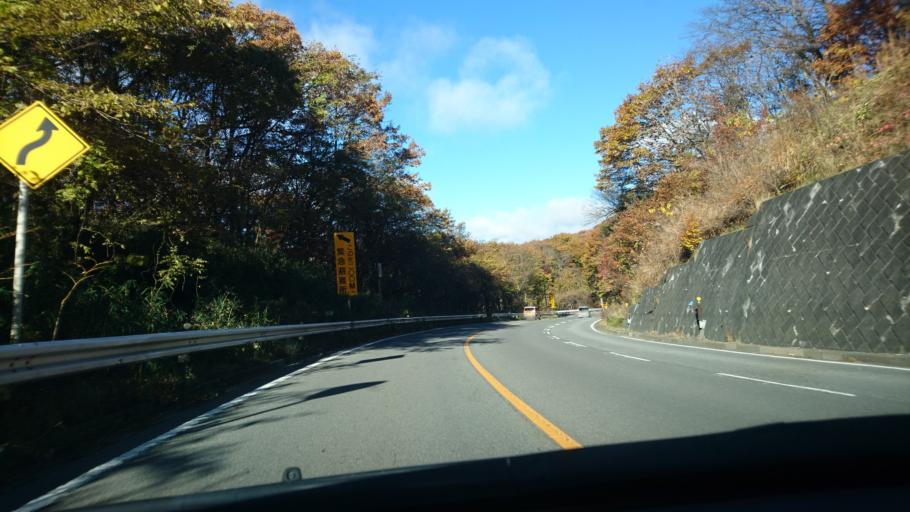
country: JP
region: Nagano
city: Saku
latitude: 36.3260
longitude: 138.6469
